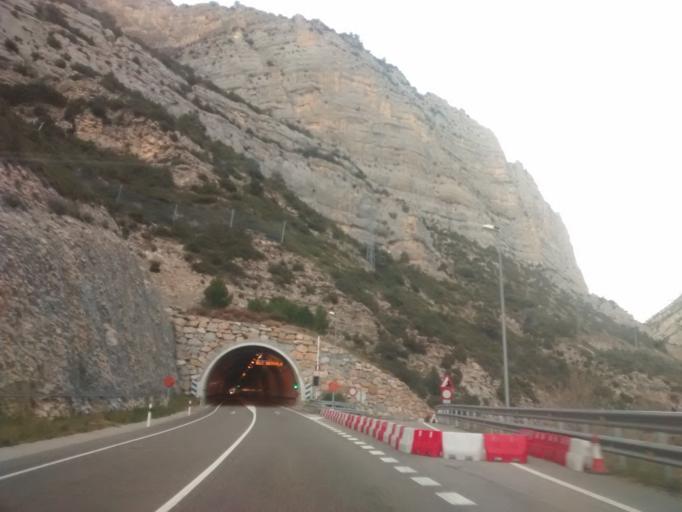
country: ES
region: Catalonia
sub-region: Provincia de Lleida
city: Coll de Nargo
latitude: 42.1347
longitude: 1.3097
